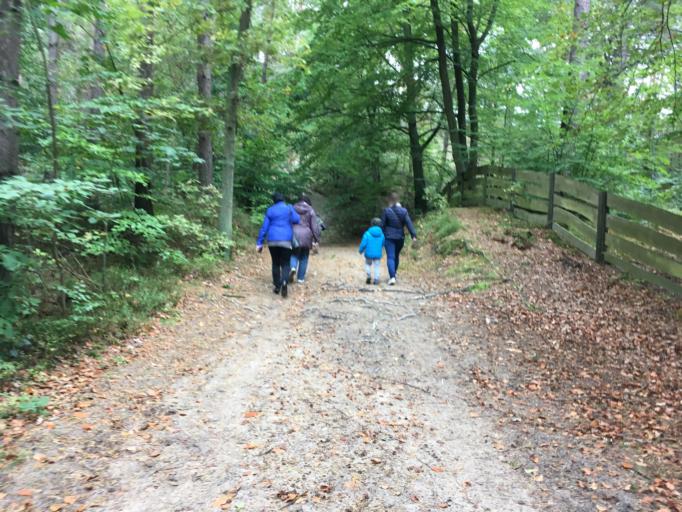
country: PL
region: Pomeranian Voivodeship
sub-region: Powiat nowodworski
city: Stegna
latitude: 54.3431
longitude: 19.1198
